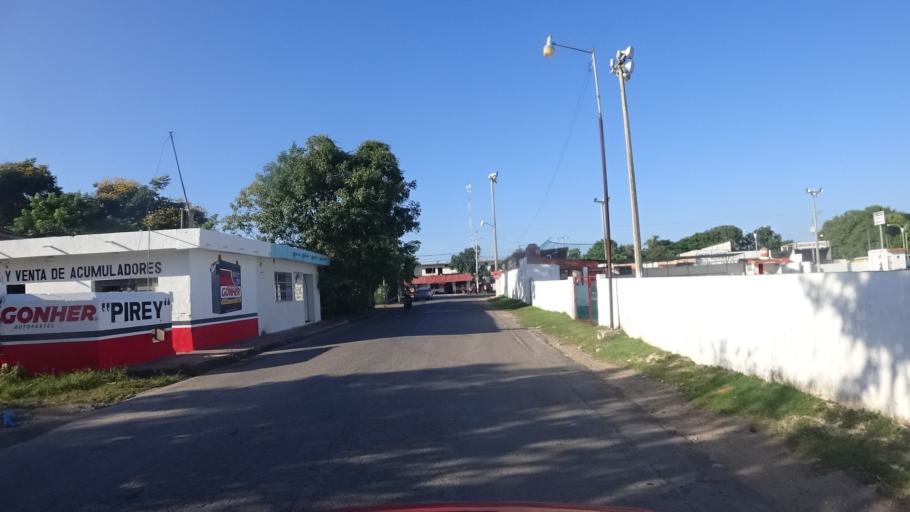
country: MX
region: Yucatan
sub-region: Tizimin
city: Tizimin
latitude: 21.1509
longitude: -88.1639
